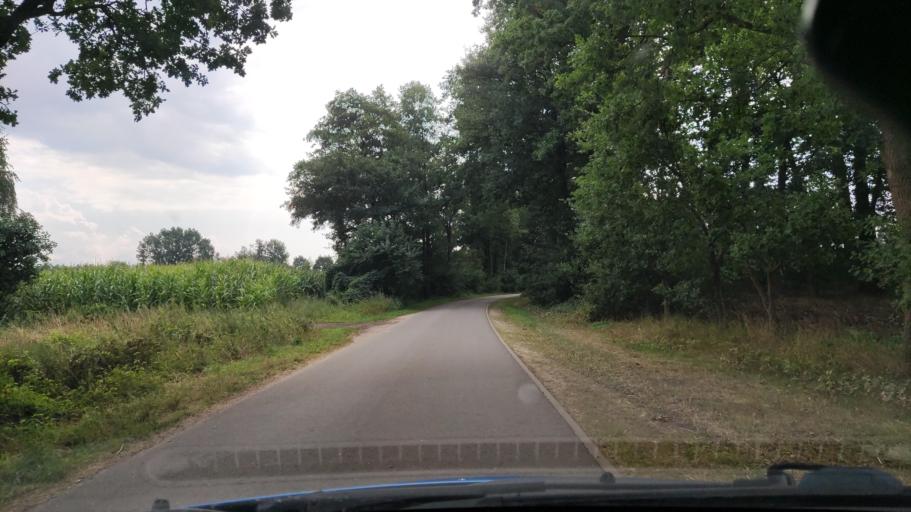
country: DE
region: Lower Saxony
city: Wittorf
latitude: 53.3449
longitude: 10.3737
